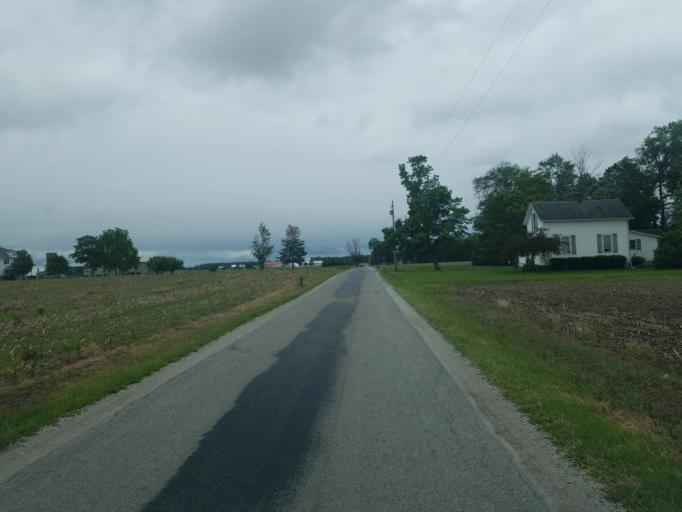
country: US
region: Ohio
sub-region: Marion County
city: Marion
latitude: 40.5613
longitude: -83.0680
